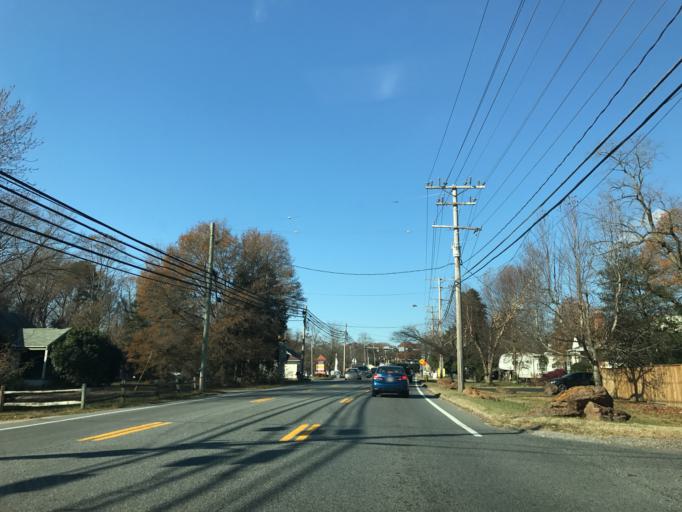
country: US
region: Maryland
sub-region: Anne Arundel County
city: Lake Shore
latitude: 39.1075
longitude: -76.4928
